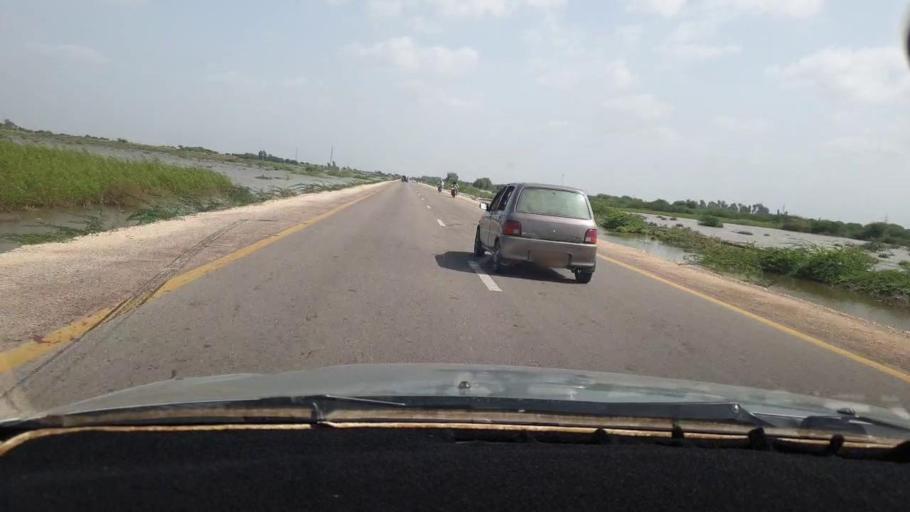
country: PK
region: Sindh
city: Digri
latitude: 25.1249
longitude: 69.1457
